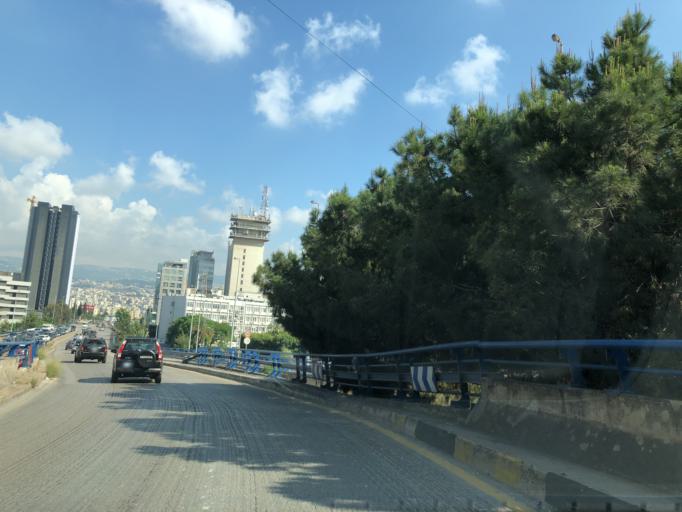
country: LB
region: Beyrouth
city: Beirut
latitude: 33.8805
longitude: 35.5192
